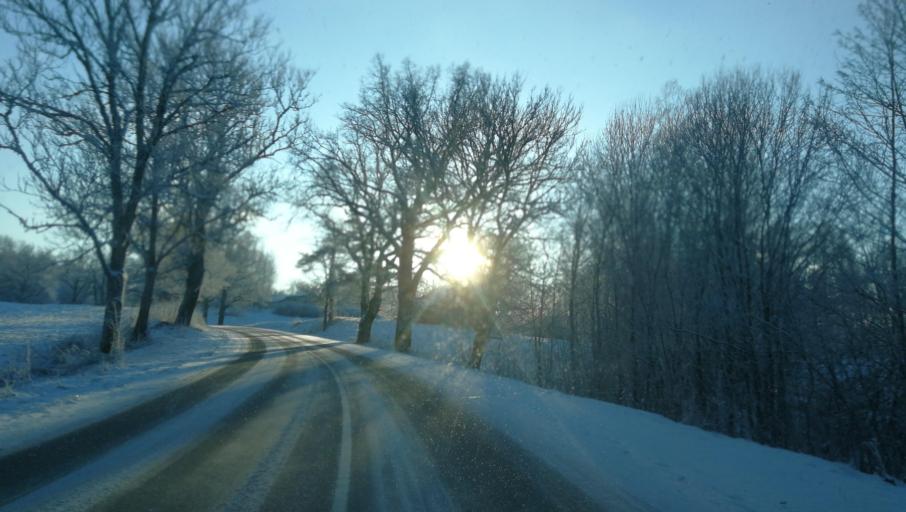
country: LV
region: Amatas Novads
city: Drabesi
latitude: 57.2482
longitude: 25.2785
